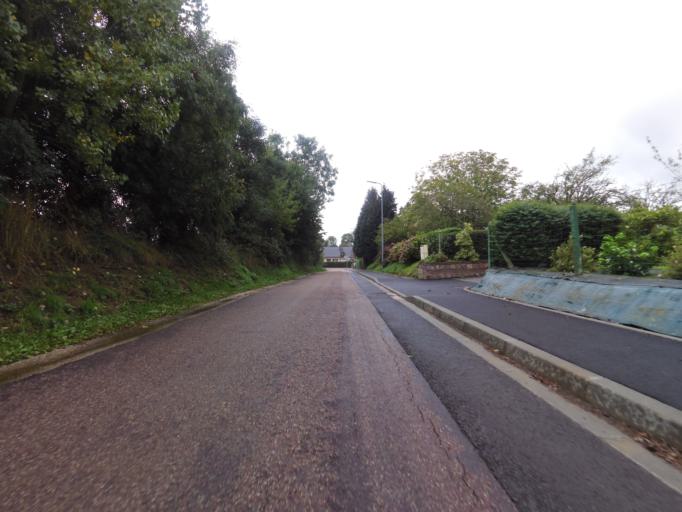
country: FR
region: Haute-Normandie
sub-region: Departement de la Seine-Maritime
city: Totes
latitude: 49.7068
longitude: 1.0258
